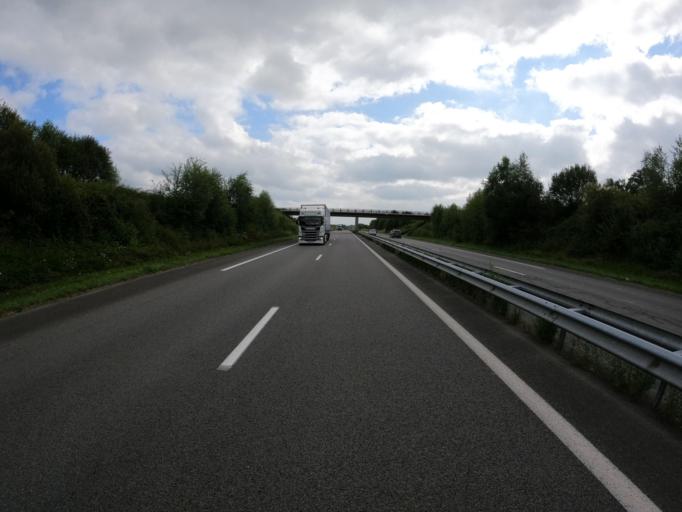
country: FR
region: Limousin
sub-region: Departement de la Haute-Vienne
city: Saint-Victurnien
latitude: 45.9063
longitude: 0.9966
